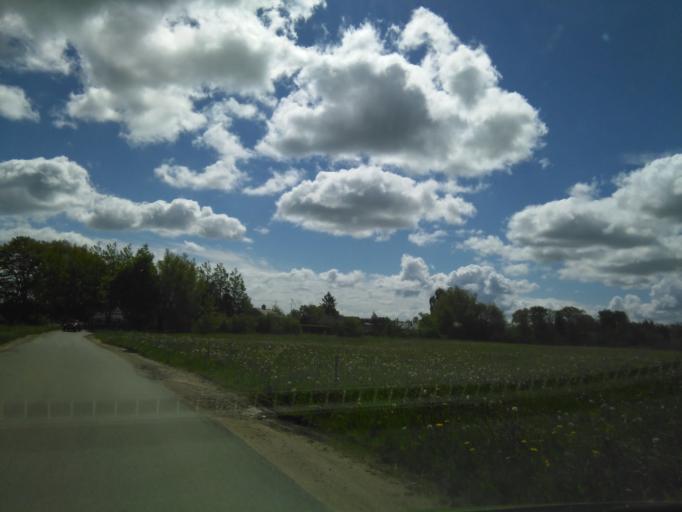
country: DK
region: Central Jutland
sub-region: Arhus Kommune
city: Beder
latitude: 56.0521
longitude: 10.2161
